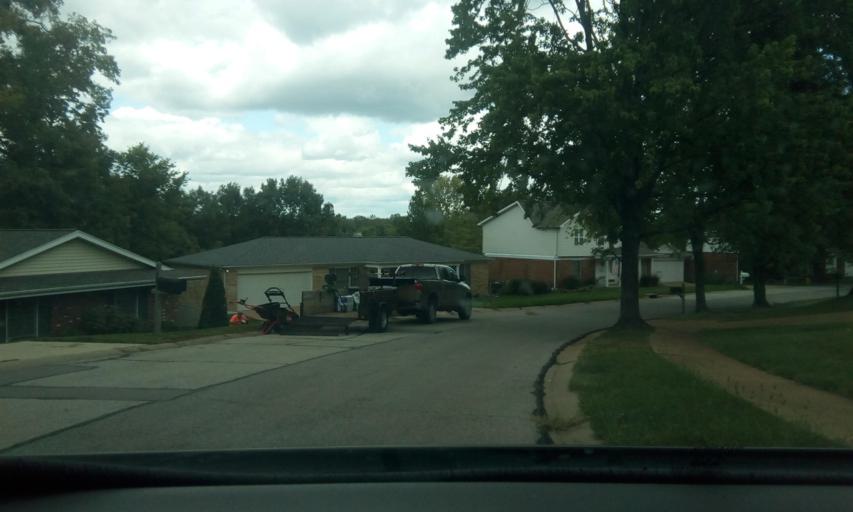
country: US
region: Missouri
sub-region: Saint Louis County
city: Ballwin
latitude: 38.6014
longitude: -90.5474
